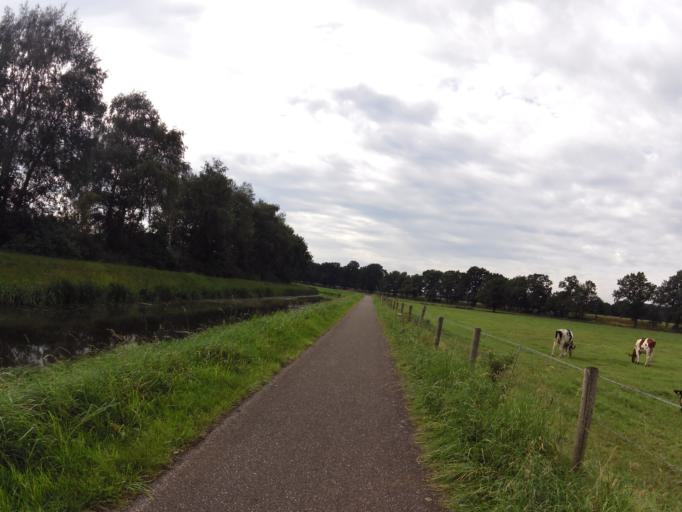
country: NL
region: Drenthe
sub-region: Gemeente Coevorden
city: Coevorden
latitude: 52.6526
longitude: 6.7862
